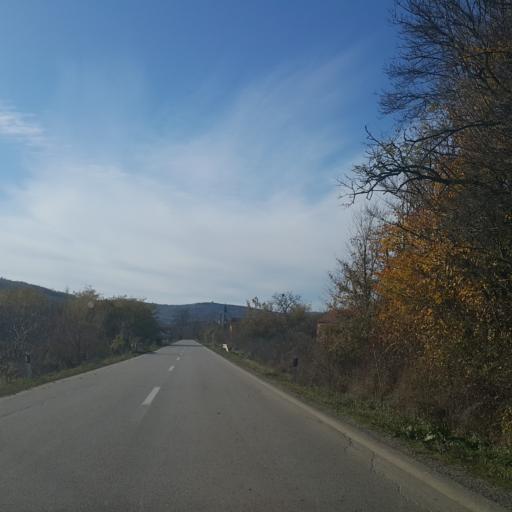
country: RS
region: Central Serbia
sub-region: Sumadijski Okrug
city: Topola
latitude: 44.2487
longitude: 20.7373
